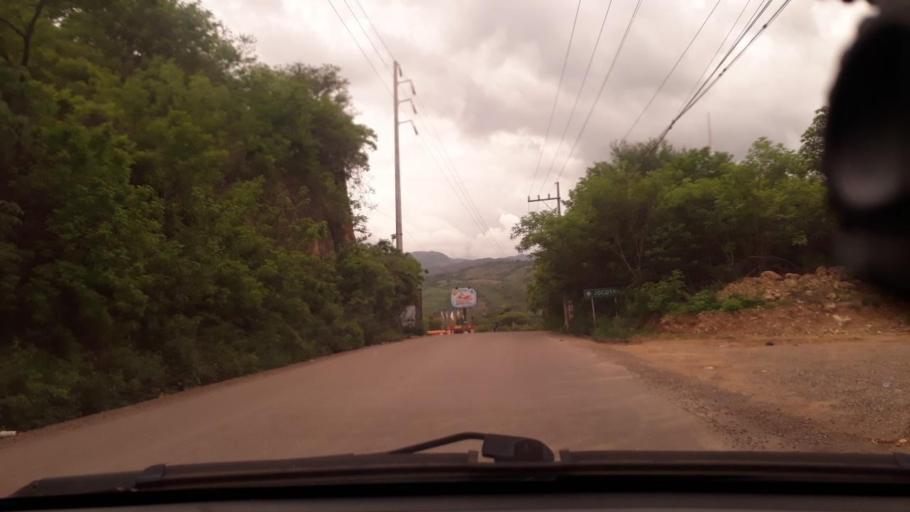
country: GT
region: Chiquimula
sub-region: Municipio de Jocotan
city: Jocotan
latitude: 14.8104
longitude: -89.3871
